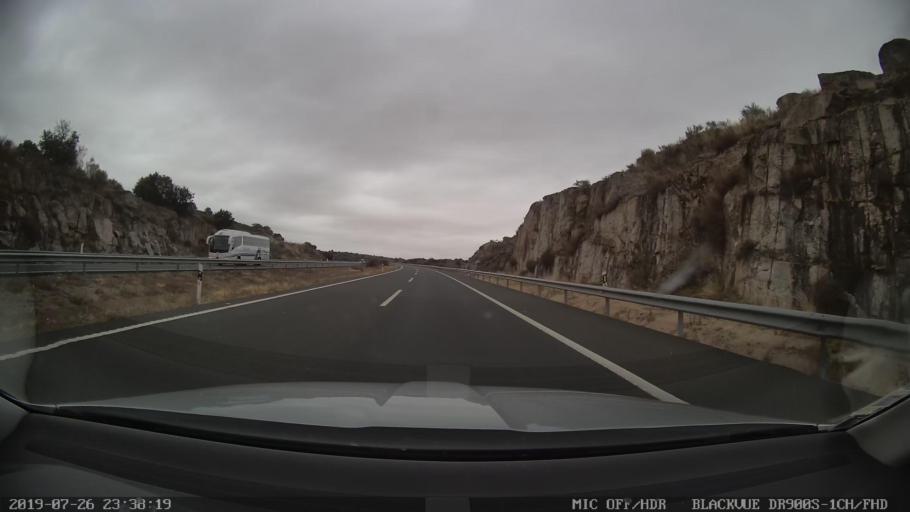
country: ES
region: Extremadura
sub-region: Provincia de Caceres
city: Trujillo
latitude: 39.4282
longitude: -5.8791
